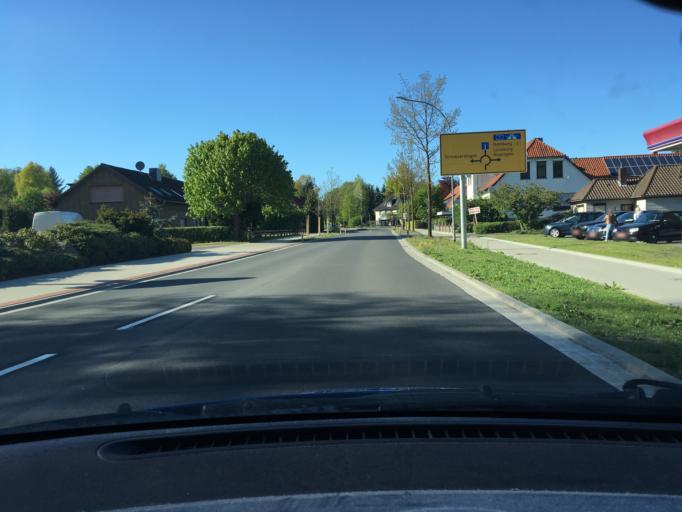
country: DE
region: Lower Saxony
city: Schneverdingen
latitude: 53.0793
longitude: 9.8632
